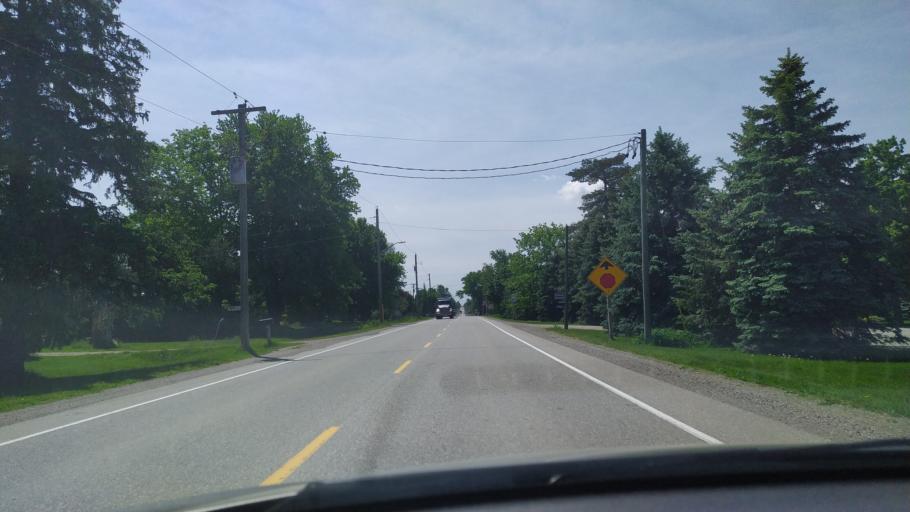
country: CA
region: Ontario
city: Dorchester
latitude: 43.1422
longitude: -81.0319
